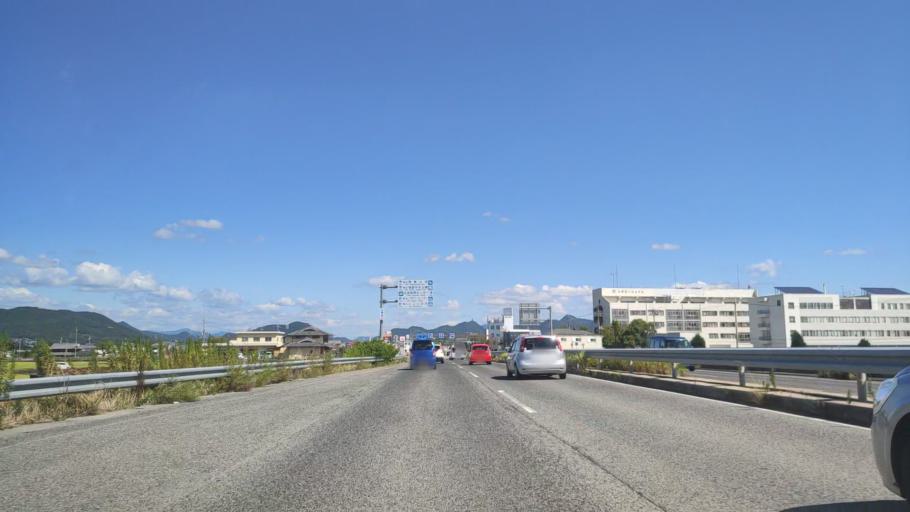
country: JP
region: Hyogo
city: Yashiro
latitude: 34.9141
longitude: 134.9559
